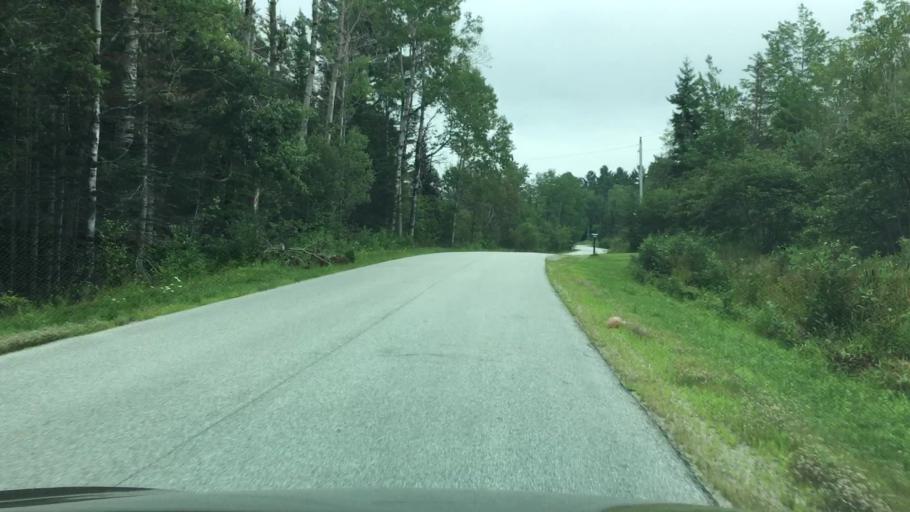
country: US
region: Maine
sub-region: Waldo County
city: Stockton Springs
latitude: 44.5279
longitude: -68.8286
